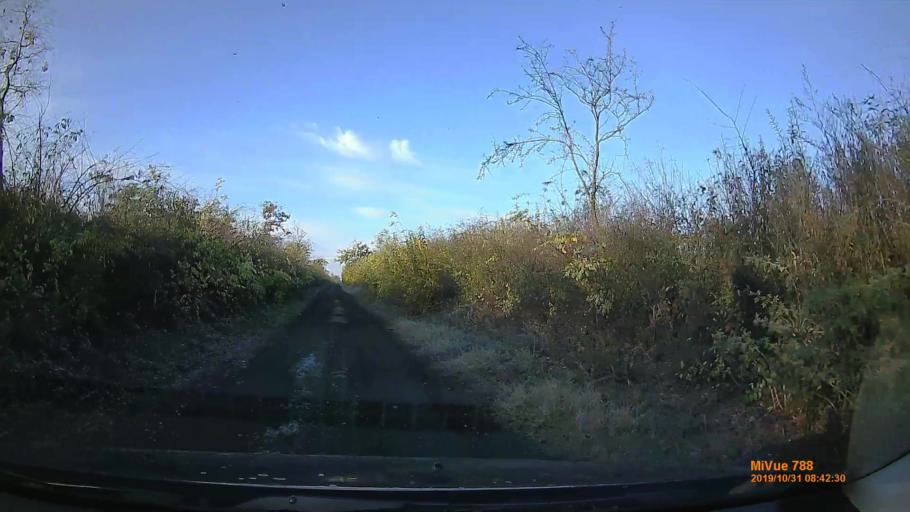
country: HU
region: Pest
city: Pand
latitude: 47.3015
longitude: 19.6339
